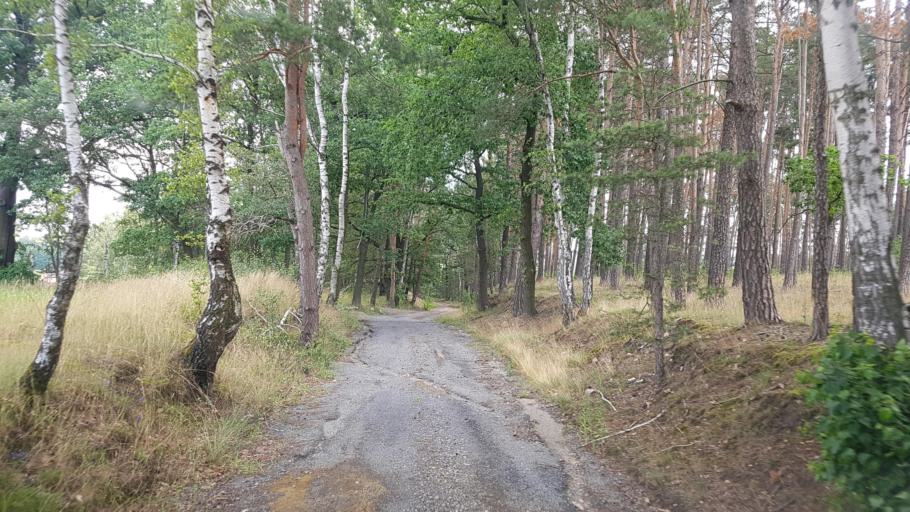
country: DE
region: Brandenburg
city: Crinitz
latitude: 51.7114
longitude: 13.8200
